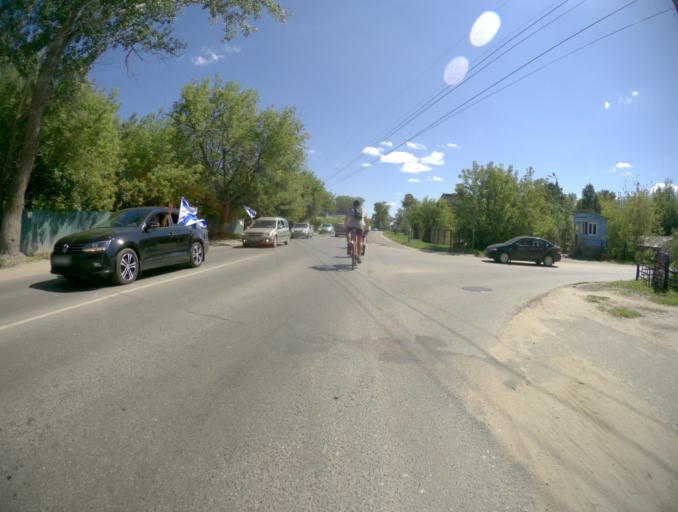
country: RU
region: Nizjnij Novgorod
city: Bor
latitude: 56.3591
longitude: 44.0697
